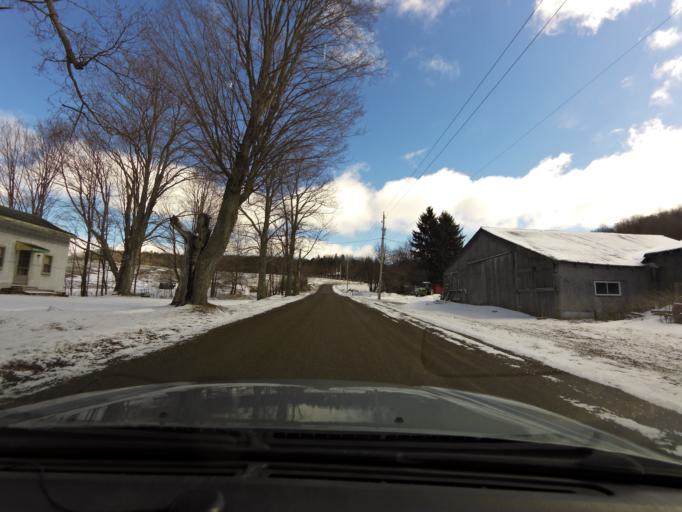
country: US
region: New York
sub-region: Cattaraugus County
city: Franklinville
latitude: 42.3482
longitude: -78.4056
